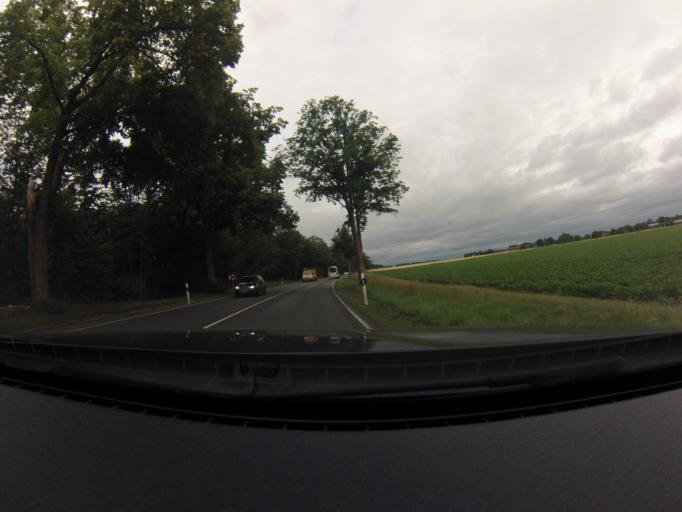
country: DE
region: North Rhine-Westphalia
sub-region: Regierungsbezirk Koln
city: Rheinbach
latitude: 50.6787
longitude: 6.9559
